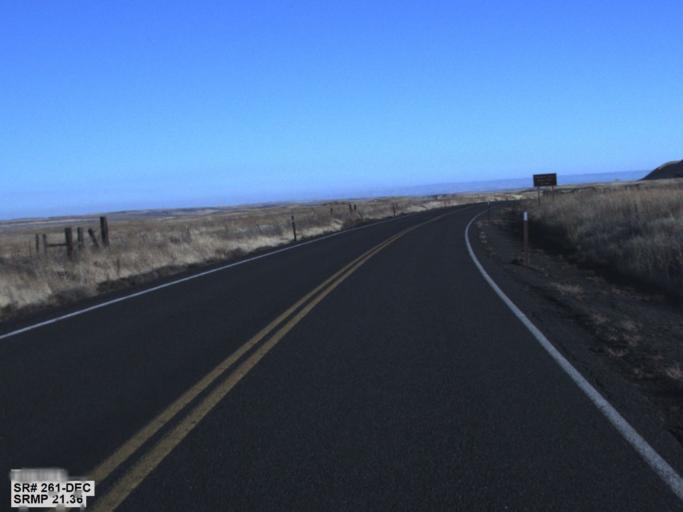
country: US
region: Washington
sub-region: Walla Walla County
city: Waitsburg
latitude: 46.6637
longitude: -118.2749
